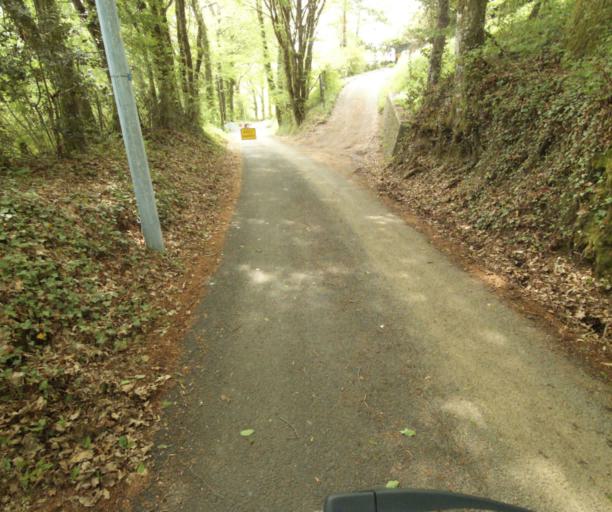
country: FR
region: Limousin
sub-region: Departement de la Correze
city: Tulle
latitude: 45.2798
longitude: 1.7762
